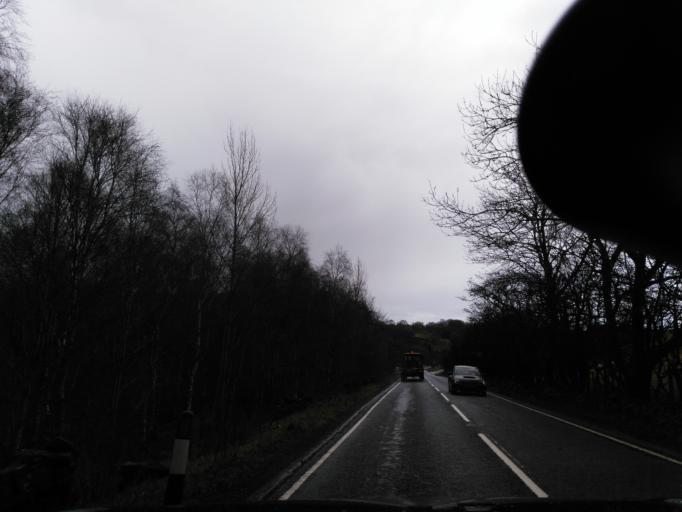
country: GB
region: England
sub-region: Bradford
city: Burley in Wharfedale
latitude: 53.9932
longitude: -1.7484
